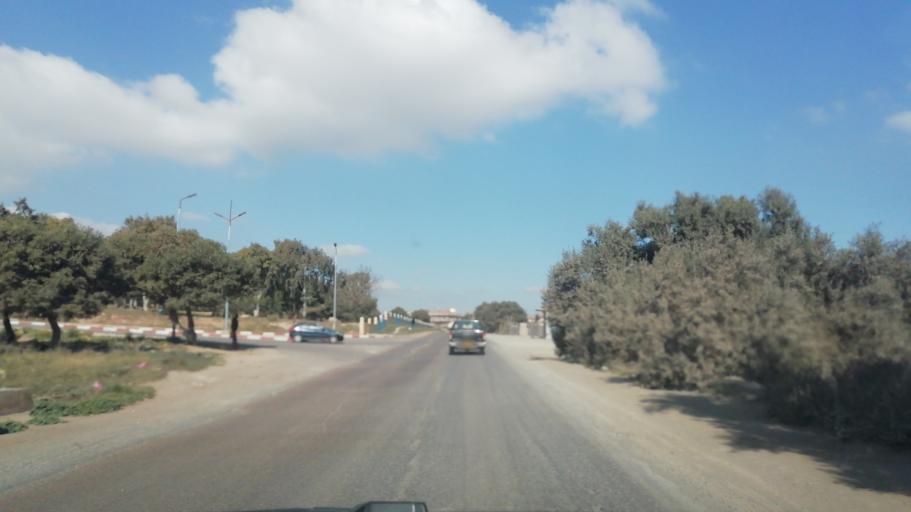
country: DZ
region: Oran
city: Ain el Bya
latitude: 35.7688
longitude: -0.2775
